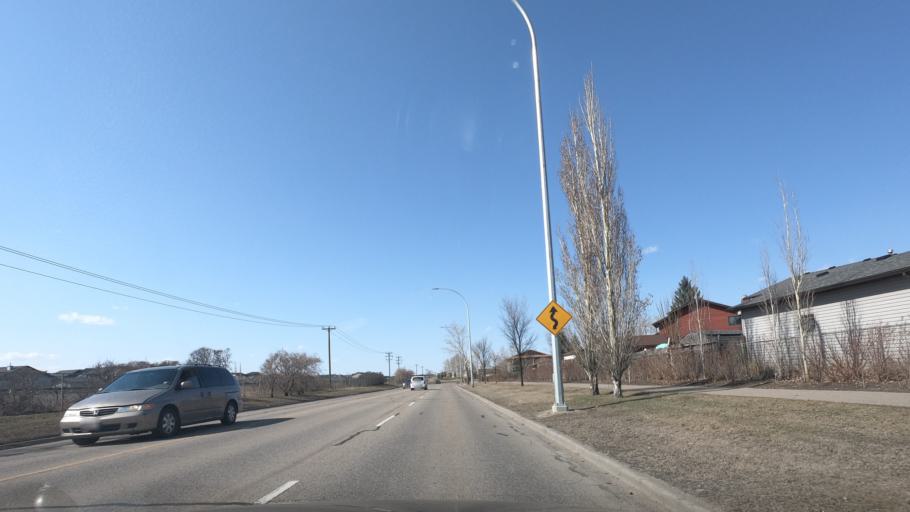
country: CA
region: Alberta
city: Airdrie
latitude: 51.2749
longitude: -114.0132
